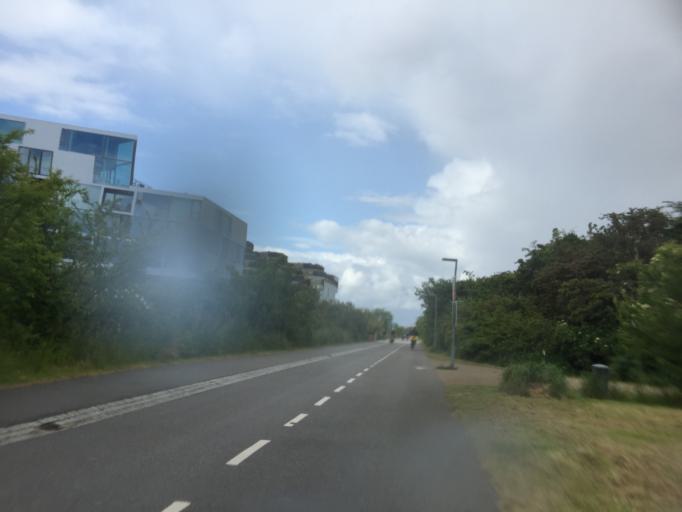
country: DK
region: Capital Region
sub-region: Tarnby Kommune
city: Tarnby
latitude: 55.6337
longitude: 12.5836
